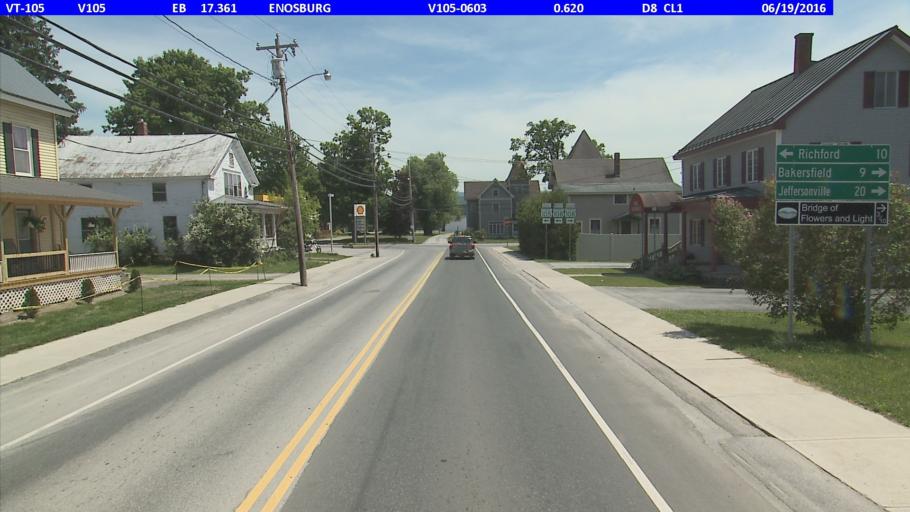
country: US
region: Vermont
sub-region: Franklin County
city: Enosburg Falls
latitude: 44.9046
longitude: -72.8076
